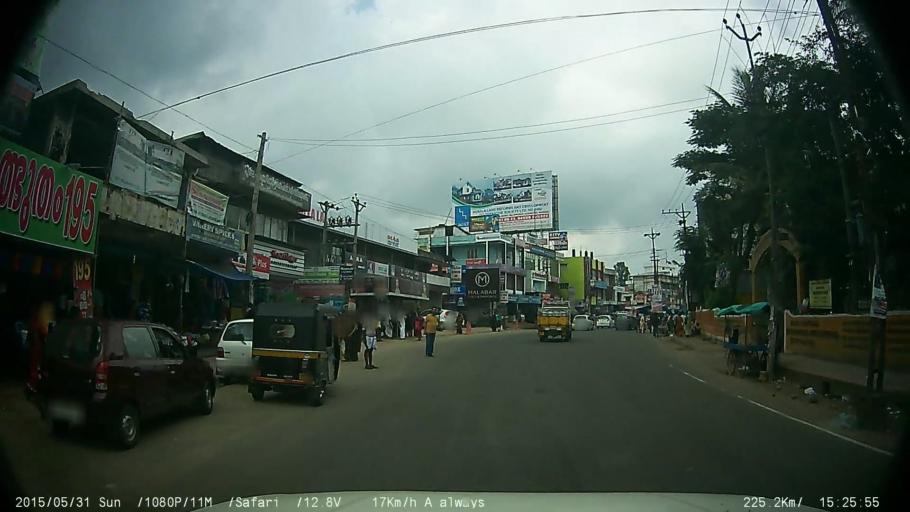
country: IN
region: Kerala
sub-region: Wayanad
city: Panamaram
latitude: 11.6630
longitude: 76.2549
